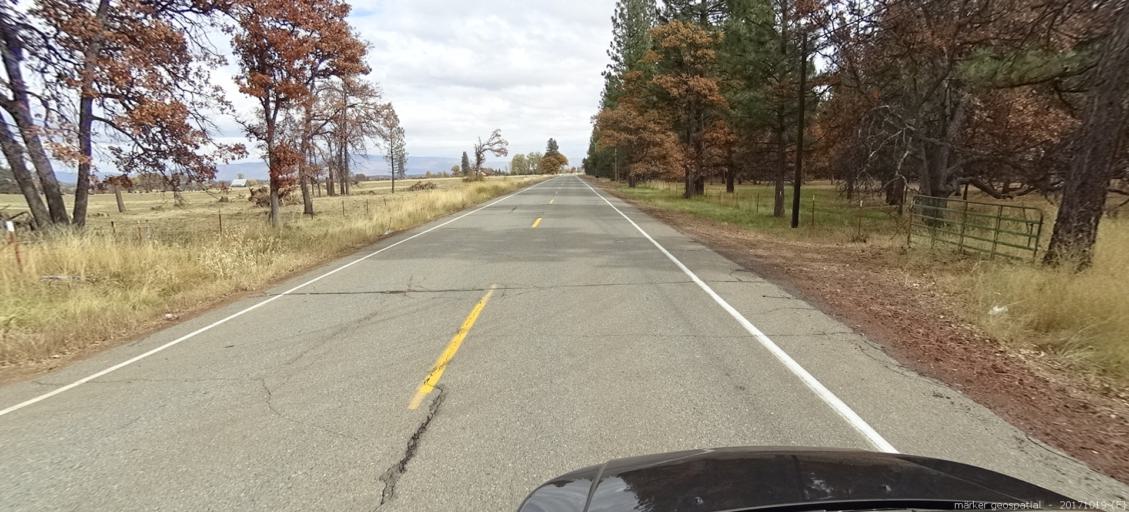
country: US
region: California
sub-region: Shasta County
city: Burney
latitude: 41.0945
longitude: -121.5243
